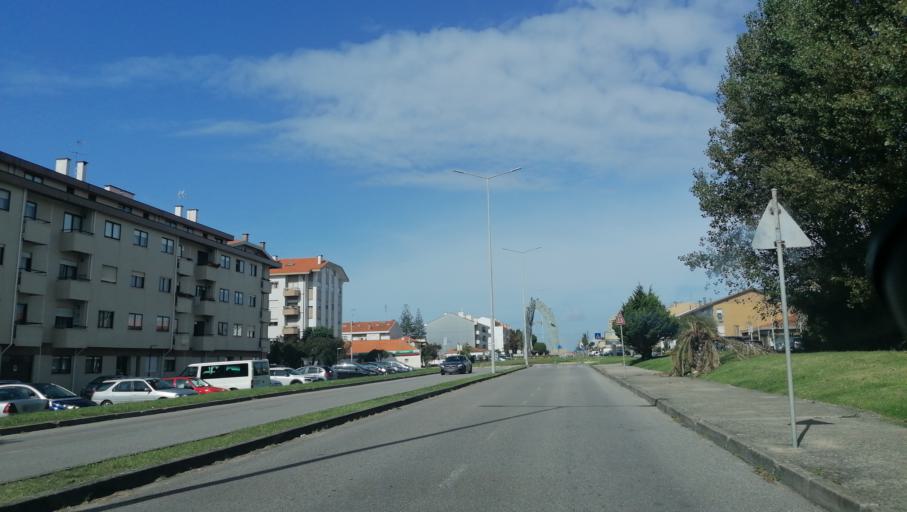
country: PT
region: Aveiro
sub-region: Espinho
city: Espinho
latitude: 41.0031
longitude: -8.6343
